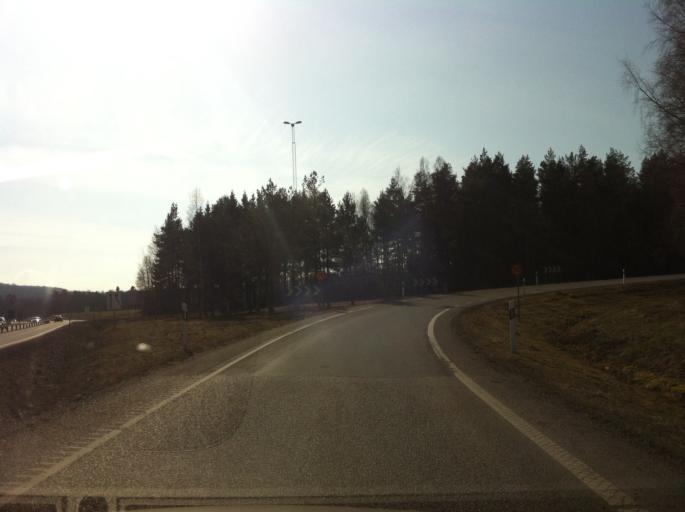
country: SE
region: Joenkoeping
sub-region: Jonkopings Kommun
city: Bankeryd
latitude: 57.8282
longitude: 14.1000
